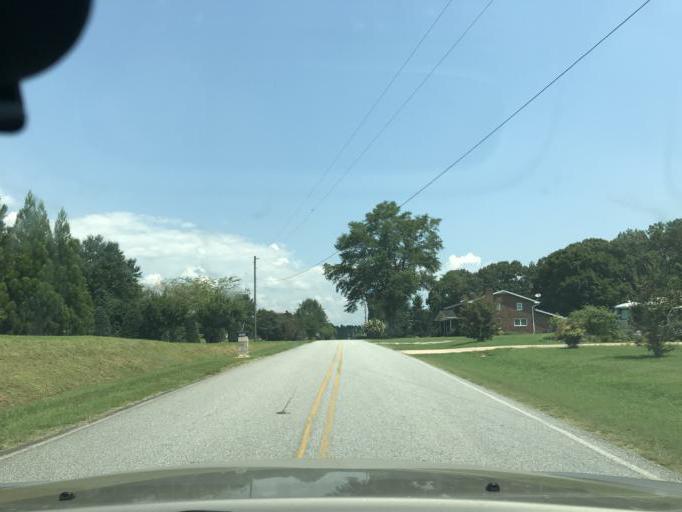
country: US
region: Georgia
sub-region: Dawson County
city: Dawsonville
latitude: 34.3347
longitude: -84.0764
